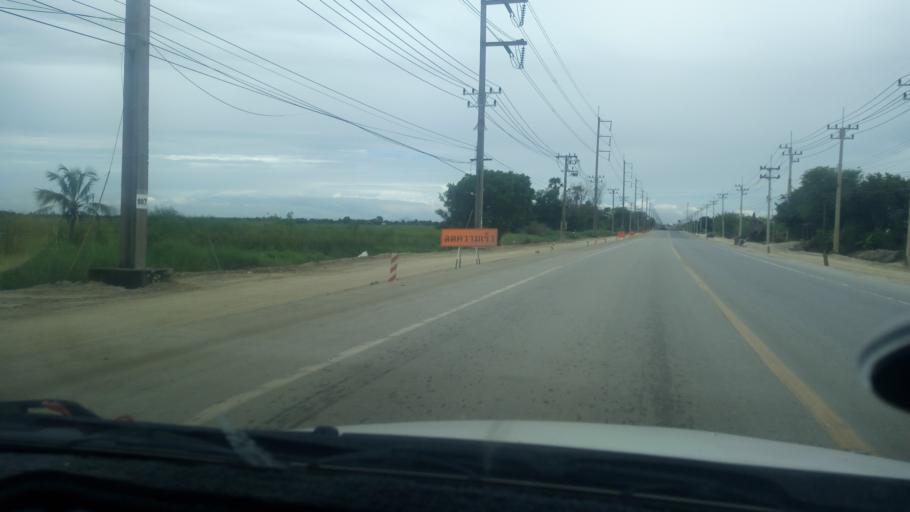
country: TH
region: Chon Buri
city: Phan Thong
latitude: 13.5251
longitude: 101.1524
